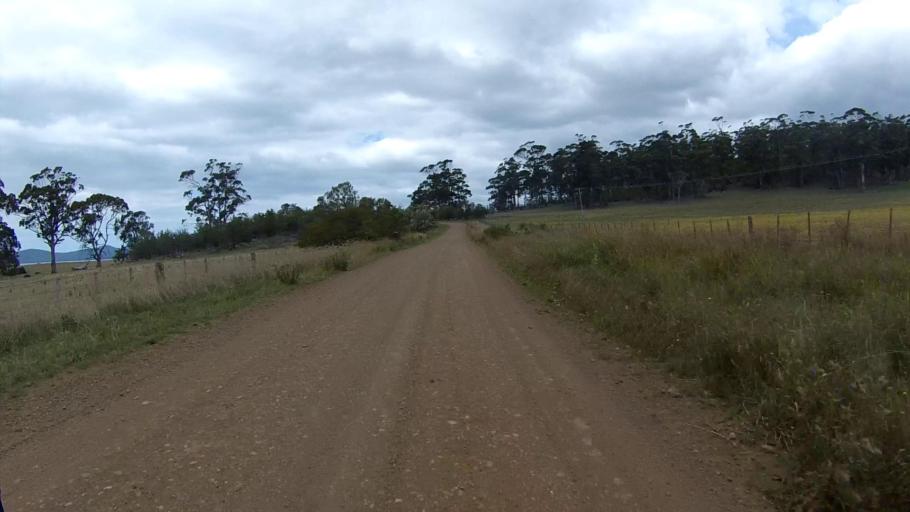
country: AU
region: Tasmania
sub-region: Sorell
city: Sorell
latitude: -42.6149
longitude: 147.9316
